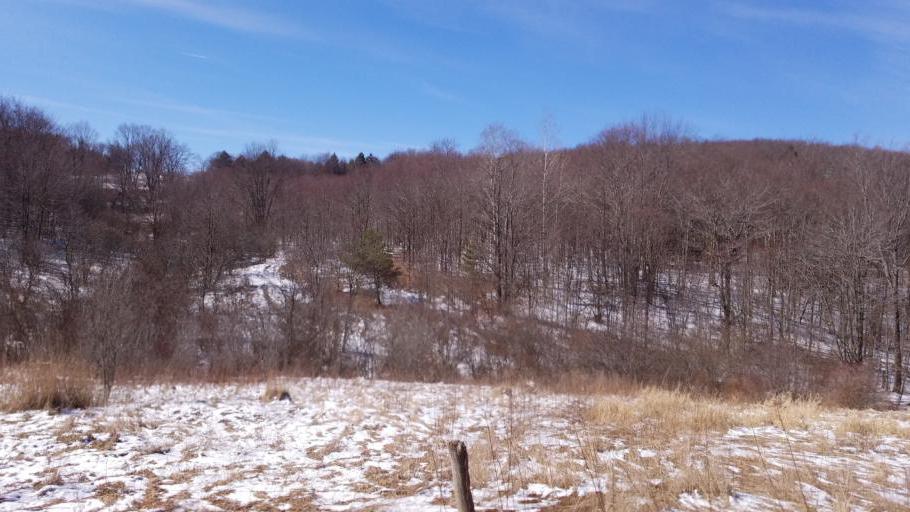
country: US
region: Pennsylvania
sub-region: Tioga County
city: Westfield
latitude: 41.9343
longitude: -77.7327
